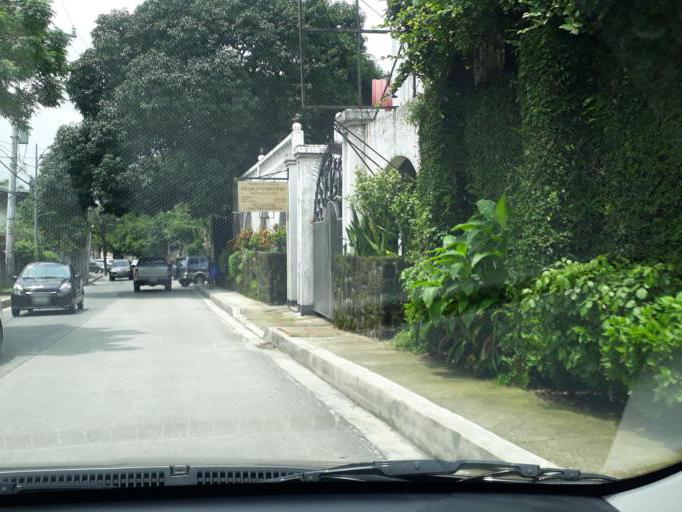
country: PH
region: Metro Manila
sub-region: San Juan
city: San Juan
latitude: 14.6214
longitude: 121.0391
